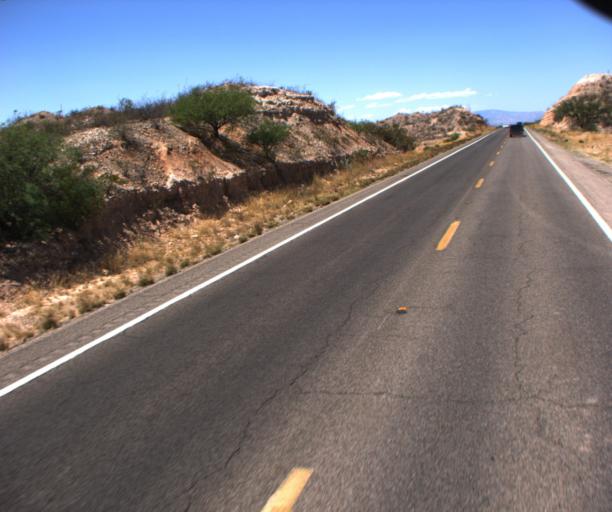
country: US
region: Arizona
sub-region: Cochise County
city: Saint David
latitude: 31.8247
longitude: -110.1760
